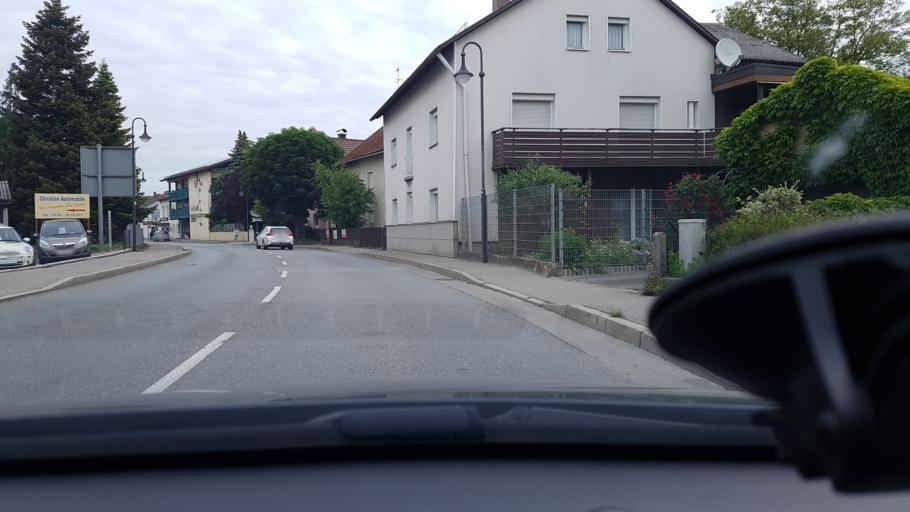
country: DE
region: Bavaria
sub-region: Lower Bavaria
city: Pocking
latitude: 48.3982
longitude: 13.3113
